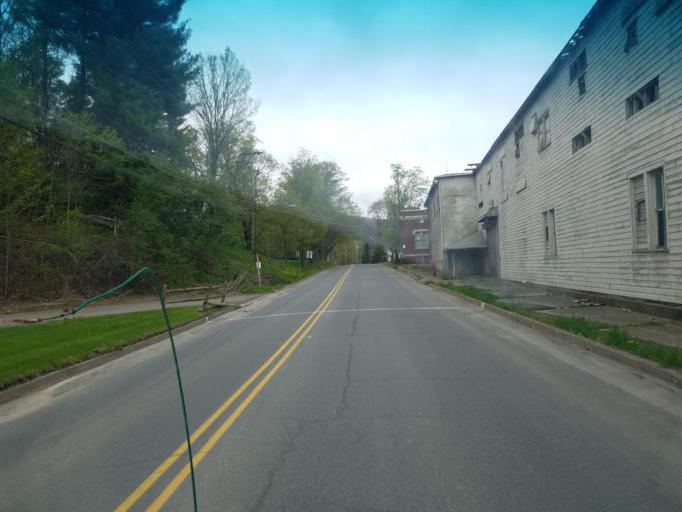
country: US
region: Pennsylvania
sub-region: Tioga County
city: Westfield
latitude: 41.9124
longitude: -77.5360
